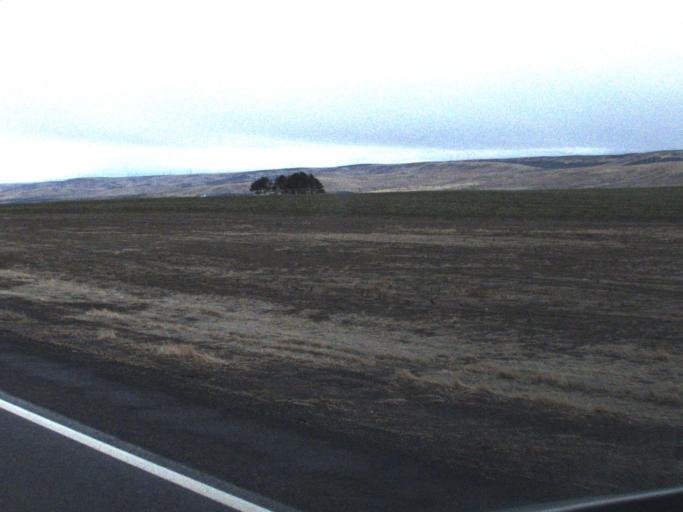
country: US
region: Washington
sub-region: Walla Walla County
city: Burbank
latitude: 46.0637
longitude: -118.7477
